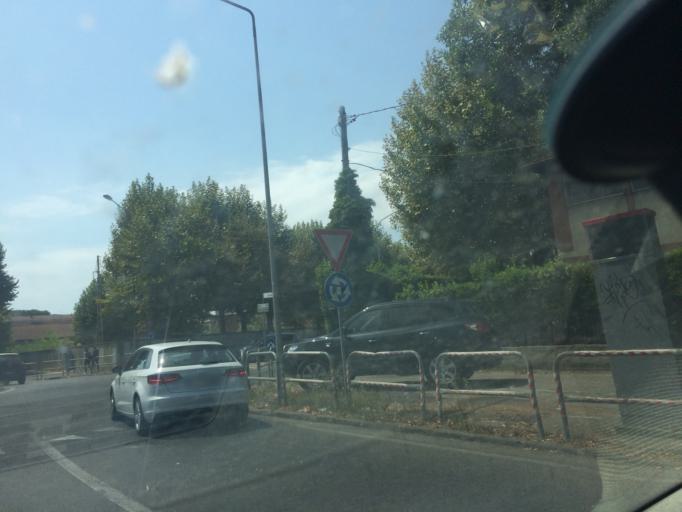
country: IT
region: Tuscany
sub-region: Provincia di Massa-Carrara
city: Carrara
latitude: 44.0479
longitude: 10.0551
